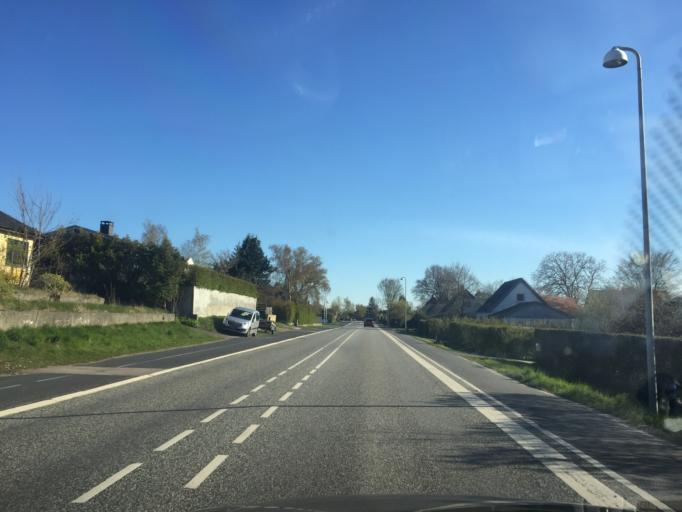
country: DK
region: Capital Region
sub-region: Halsnaes Kommune
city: Frederiksvaerk
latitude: 55.9955
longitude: 12.0138
